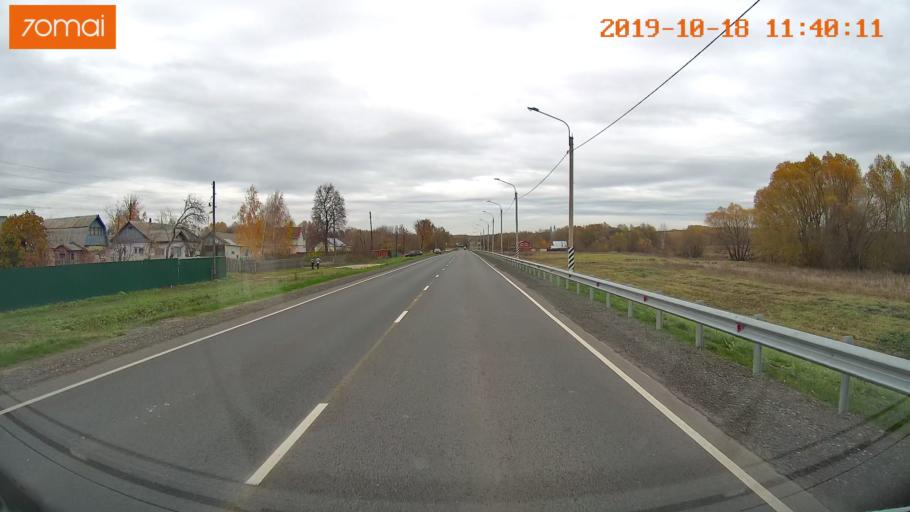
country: RU
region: Rjazan
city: Oktyabr'skiy
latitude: 54.1781
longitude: 38.8870
